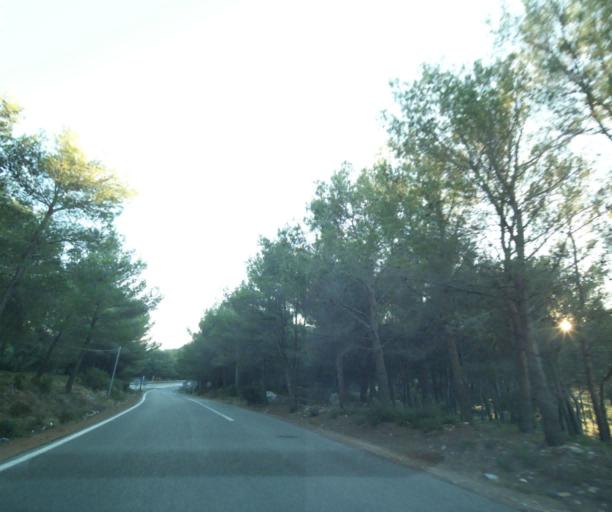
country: FR
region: Provence-Alpes-Cote d'Azur
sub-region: Departement des Bouches-du-Rhone
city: Roquefort-la-Bedoule
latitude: 43.2243
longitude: 5.5808
